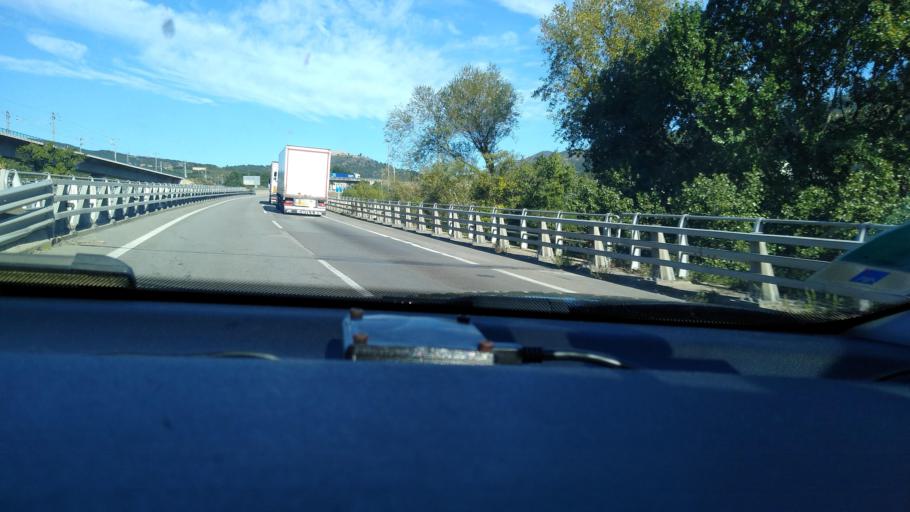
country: ES
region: Catalonia
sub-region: Provincia de Girona
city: la Jonquera
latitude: 42.4291
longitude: 2.8643
